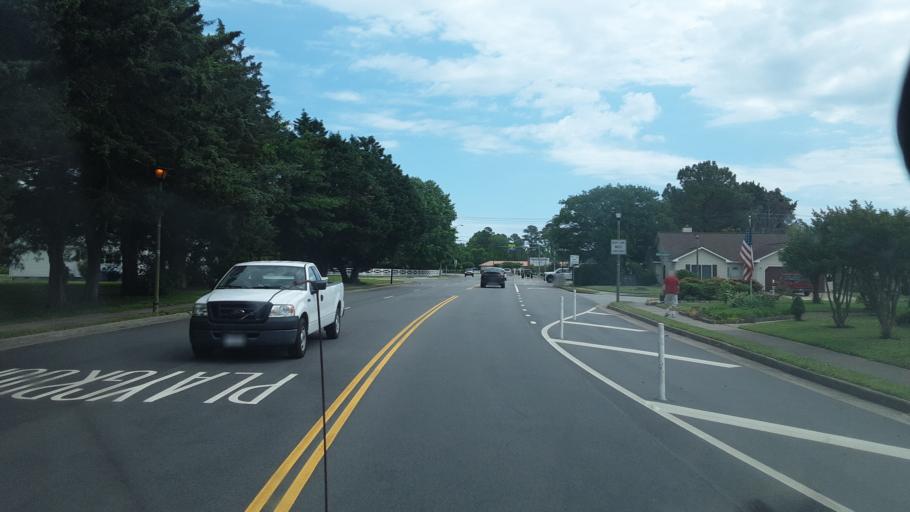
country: US
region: Virginia
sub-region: City of Virginia Beach
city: Virginia Beach
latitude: 36.7819
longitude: -75.9953
